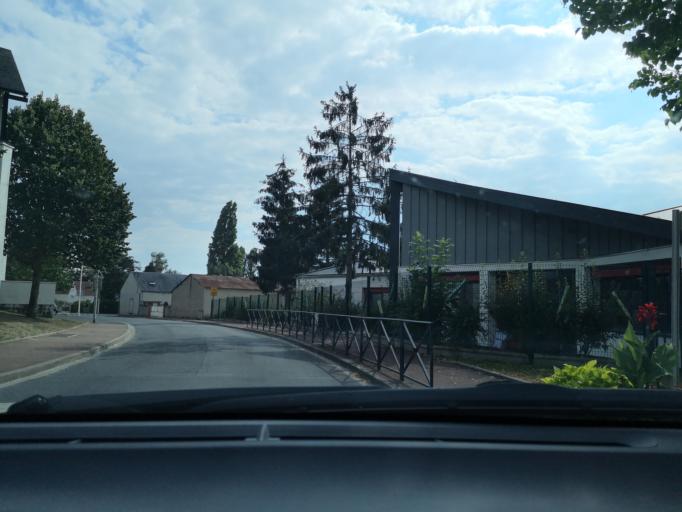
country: FR
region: Centre
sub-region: Departement du Loiret
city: Semoy
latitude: 47.9330
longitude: 1.9478
